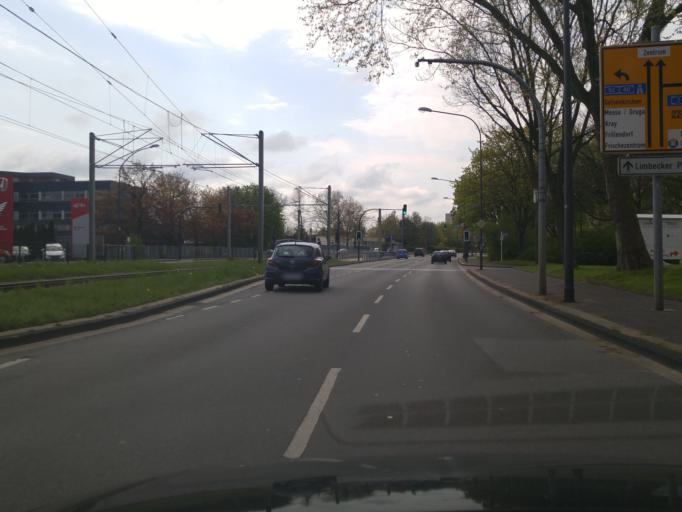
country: DE
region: North Rhine-Westphalia
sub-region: Regierungsbezirk Dusseldorf
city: Essen
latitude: 51.4713
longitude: 7.0172
